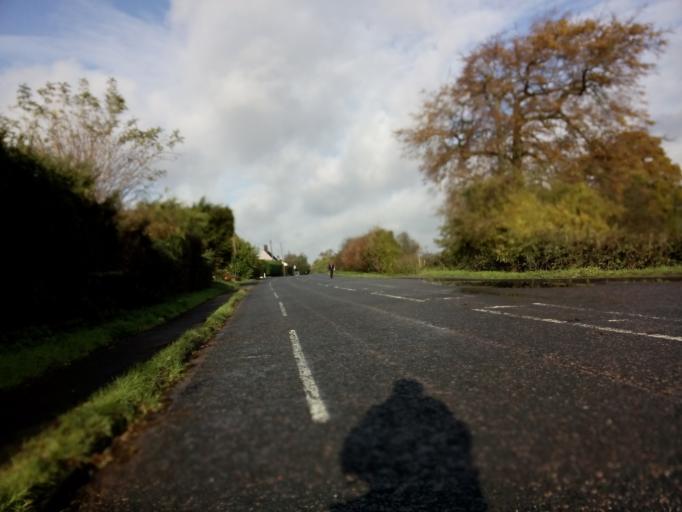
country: GB
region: England
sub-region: Suffolk
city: Bramford
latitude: 52.0889
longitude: 1.1222
